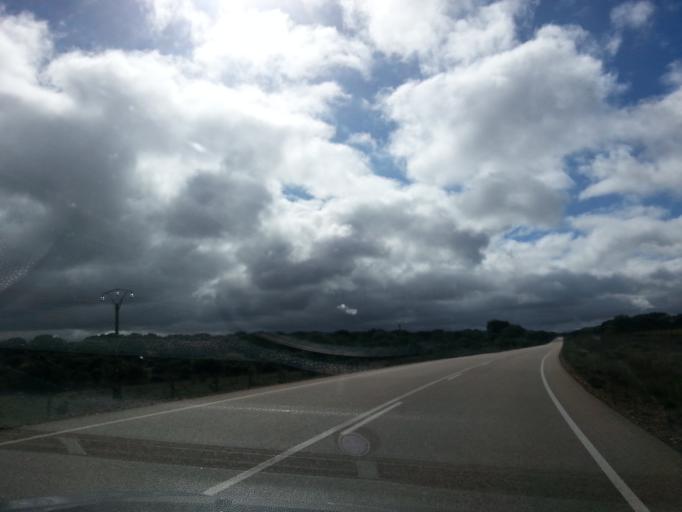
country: ES
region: Castille and Leon
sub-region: Provincia de Salamanca
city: Abusejo
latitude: 40.6951
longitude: -6.1322
